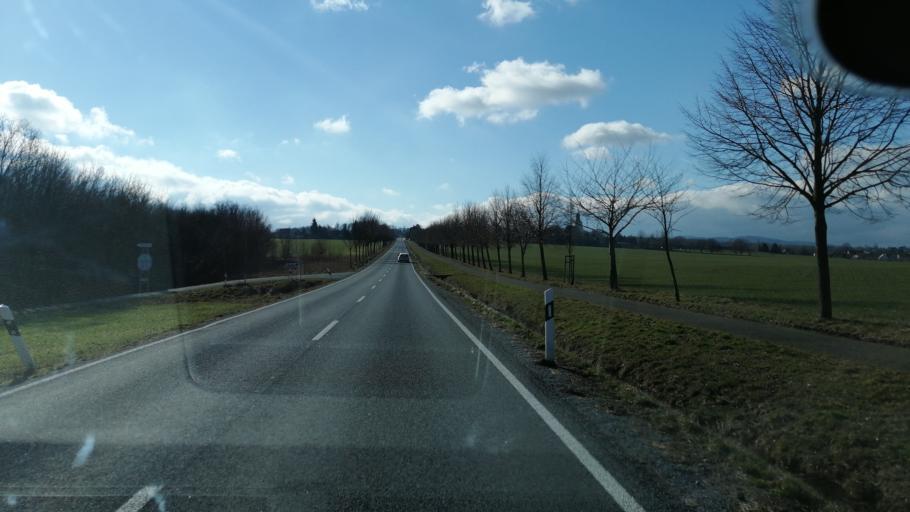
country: DE
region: Saxony
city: Lobau
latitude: 51.1359
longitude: 14.6882
